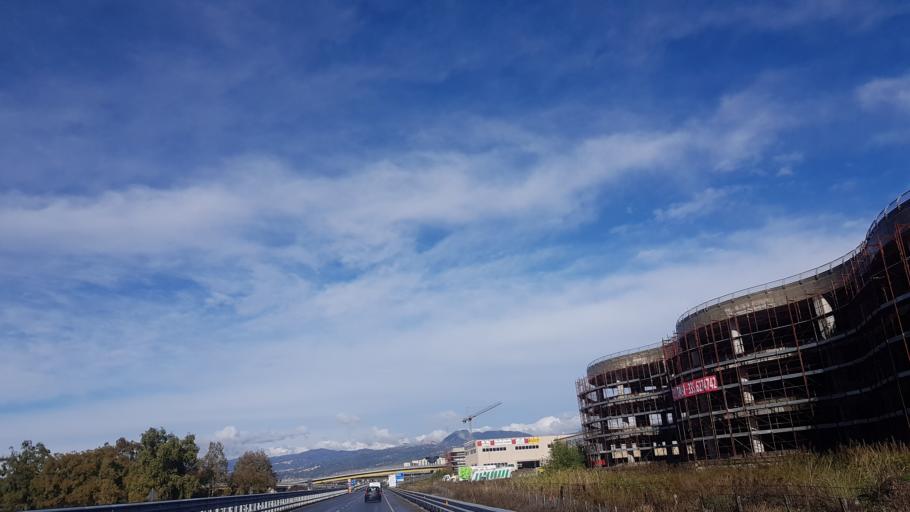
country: IT
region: Calabria
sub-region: Provincia di Catanzaro
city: Roccelletta
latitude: 38.8458
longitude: 16.5826
